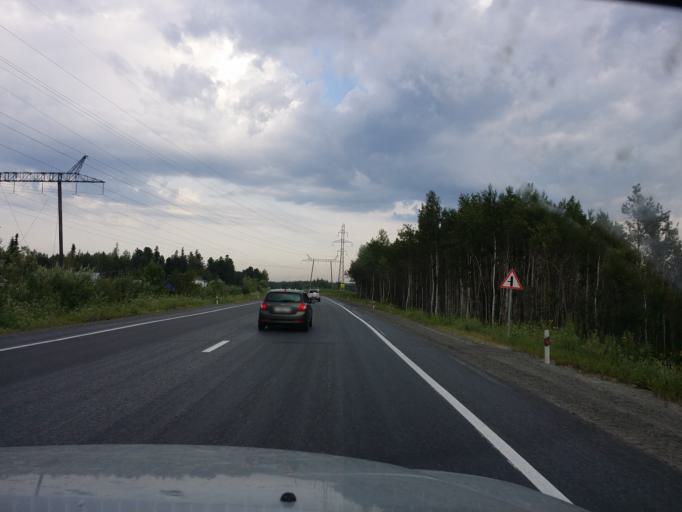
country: RU
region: Khanty-Mansiyskiy Avtonomnyy Okrug
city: Nizhnevartovsk
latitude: 61.0434
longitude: 76.3504
